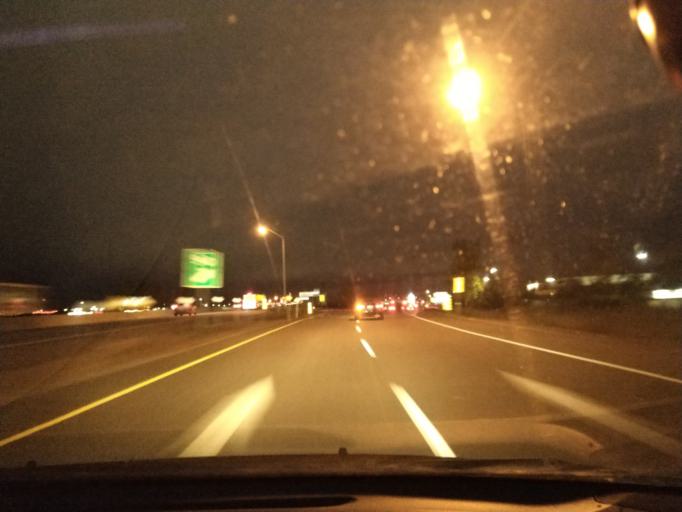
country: CA
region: Ontario
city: Innisfil
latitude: 44.3322
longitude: -79.6837
